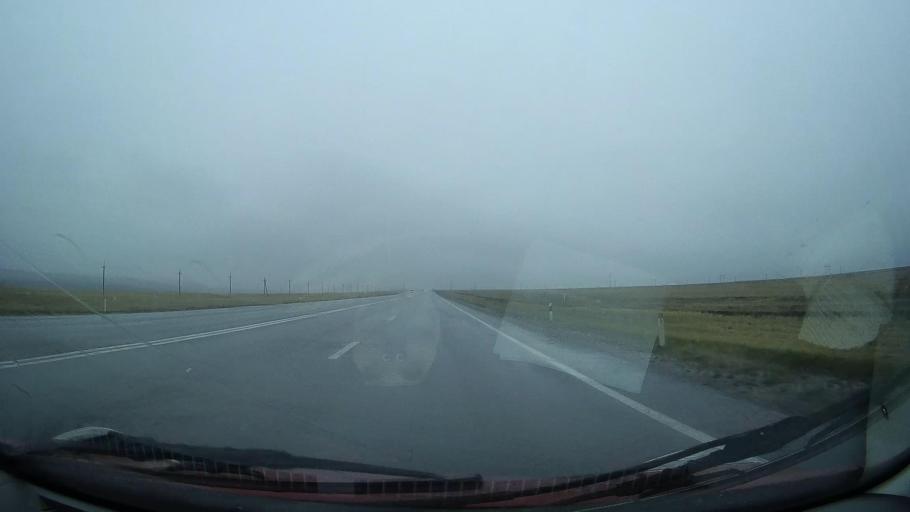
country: RU
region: Stavropol'skiy
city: Kursavka
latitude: 44.5801
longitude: 42.2473
